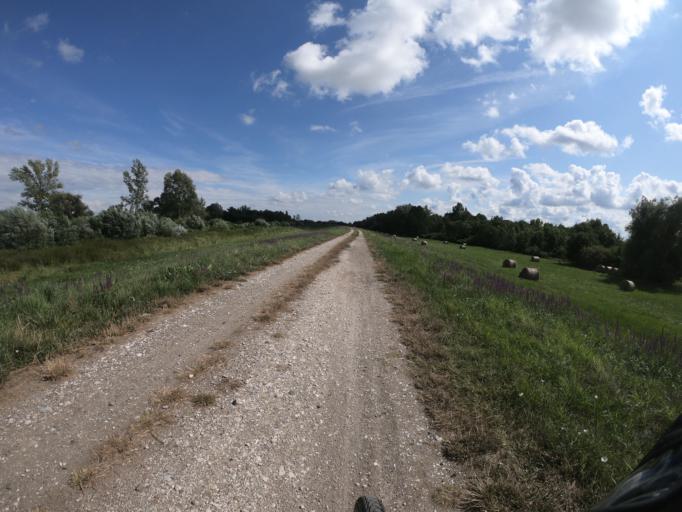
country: HU
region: Heves
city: Poroszlo
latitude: 47.6961
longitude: 20.6852
